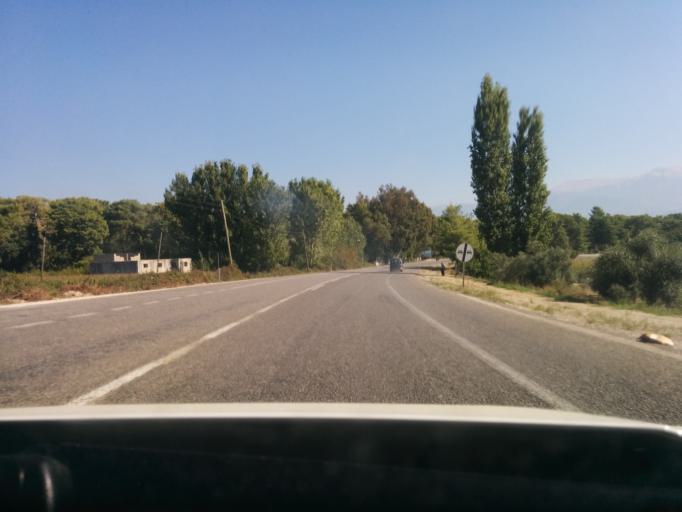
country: TR
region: Mugla
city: Esen
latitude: 36.4688
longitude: 29.2920
